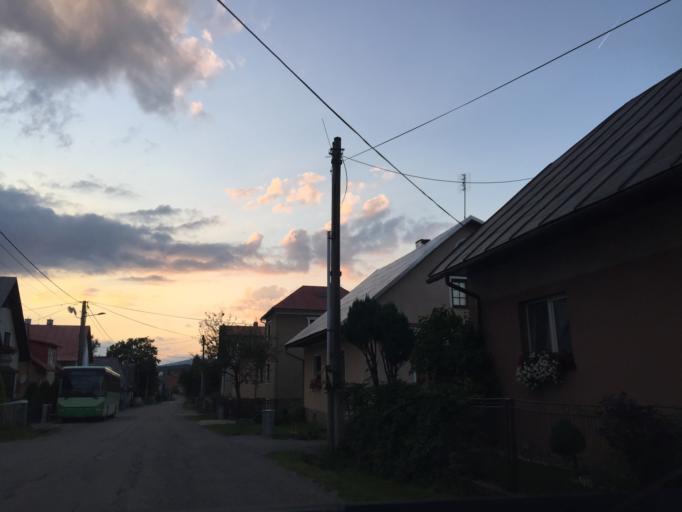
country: PL
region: Silesian Voivodeship
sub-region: Powiat zywiecki
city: Sopotnia Wielka
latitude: 49.4653
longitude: 19.3142
